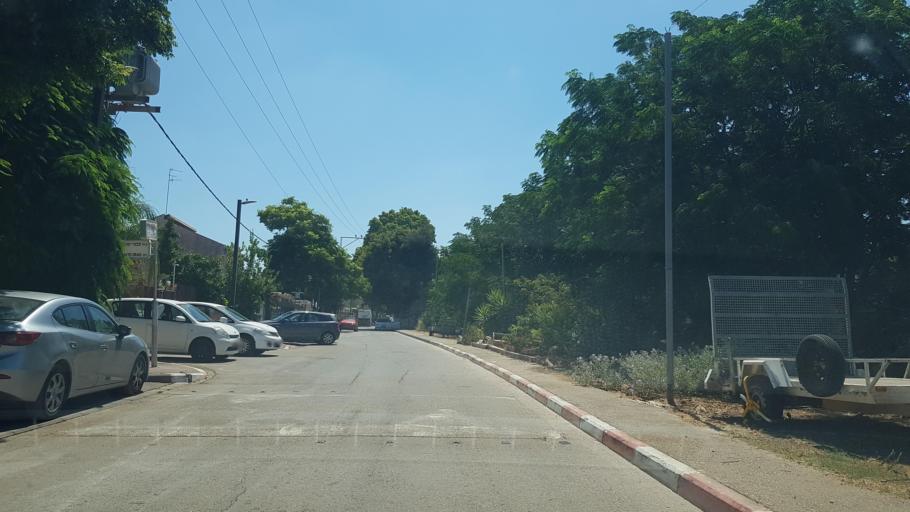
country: IL
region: Tel Aviv
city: Ramat HaSharon
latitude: 32.1540
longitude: 34.8338
